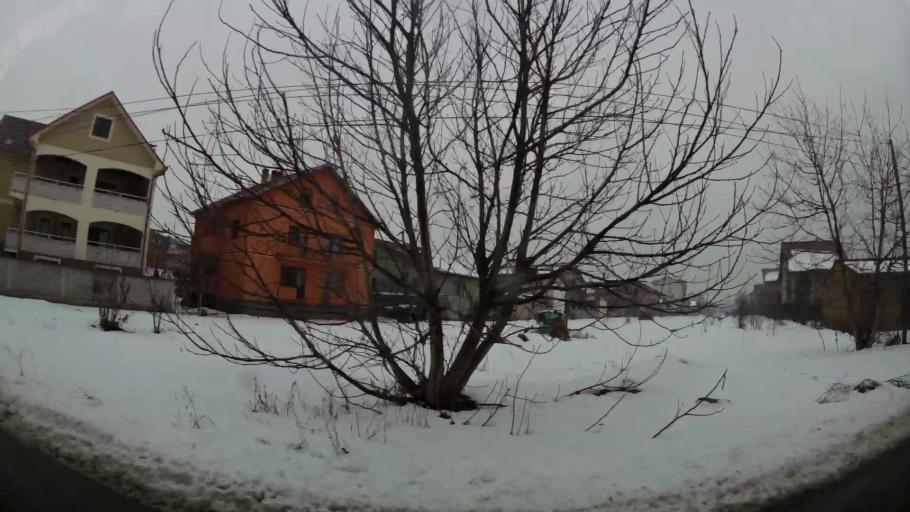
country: RS
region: Central Serbia
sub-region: Belgrade
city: Zemun
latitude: 44.8536
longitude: 20.3518
